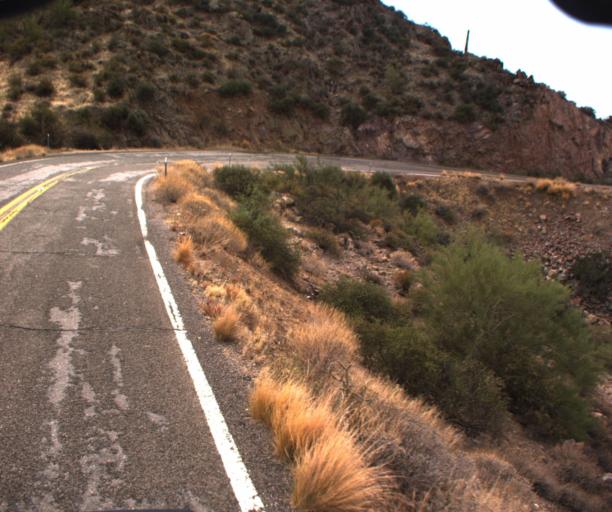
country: US
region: Arizona
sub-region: Pinal County
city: Apache Junction
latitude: 33.5089
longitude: -111.4561
